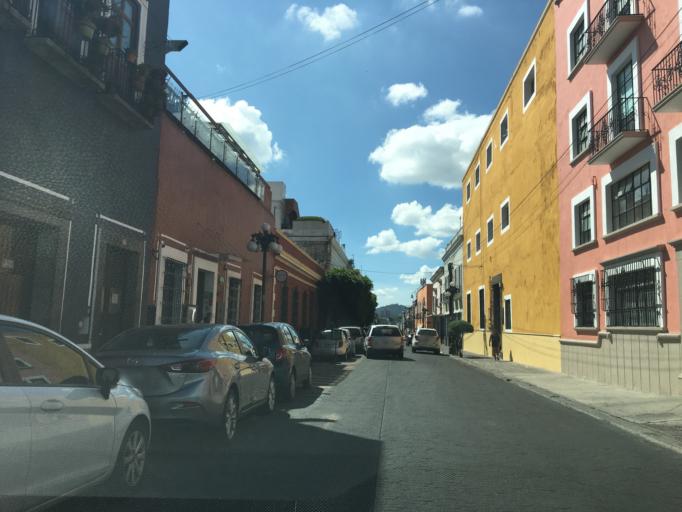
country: MX
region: Puebla
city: Puebla
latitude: 19.0410
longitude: -98.1997
